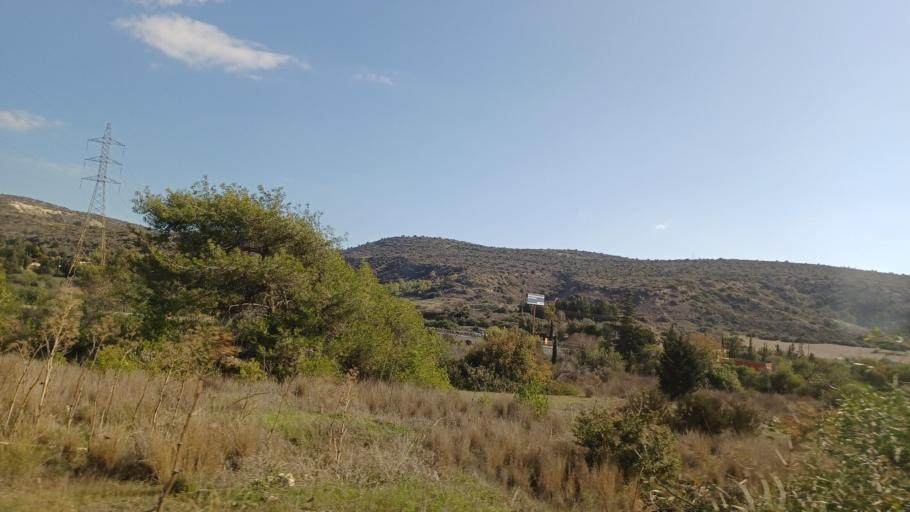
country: CY
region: Limassol
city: Pyrgos
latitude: 34.7234
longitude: 33.2029
